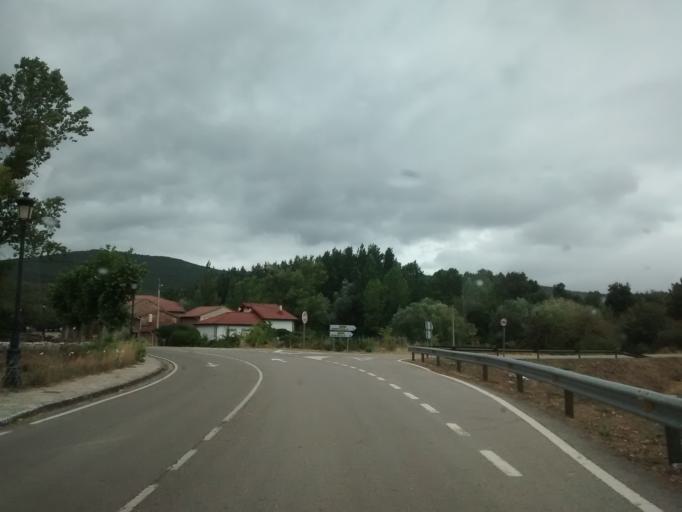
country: ES
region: Castille and Leon
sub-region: Provincia de Palencia
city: Berzosilla
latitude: 42.7951
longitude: -3.9840
